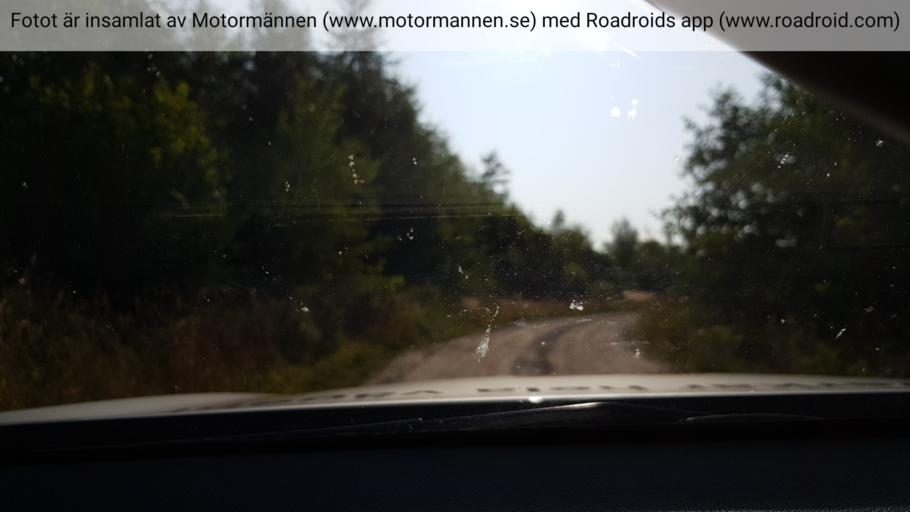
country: SE
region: Stockholm
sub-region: Nynashamns Kommun
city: Nynashamn
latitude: 58.9348
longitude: 17.9098
